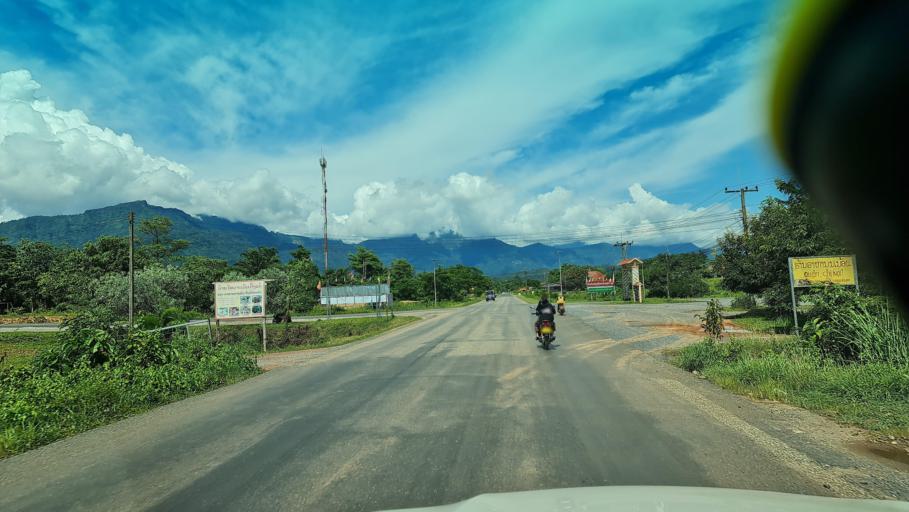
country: LA
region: Bolikhamxai
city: Ban Nahin
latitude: 18.3004
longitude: 104.1184
